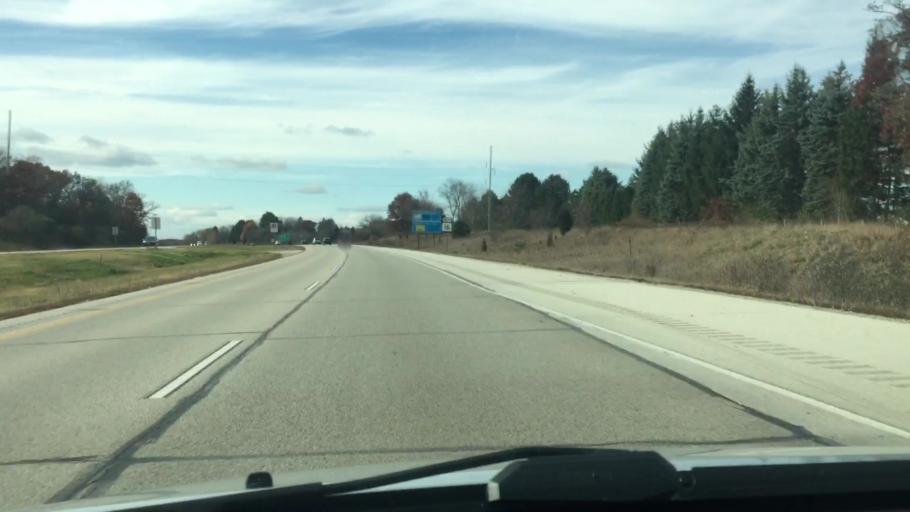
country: US
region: Wisconsin
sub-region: Waukesha County
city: Hartland
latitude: 43.1084
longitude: -88.3211
